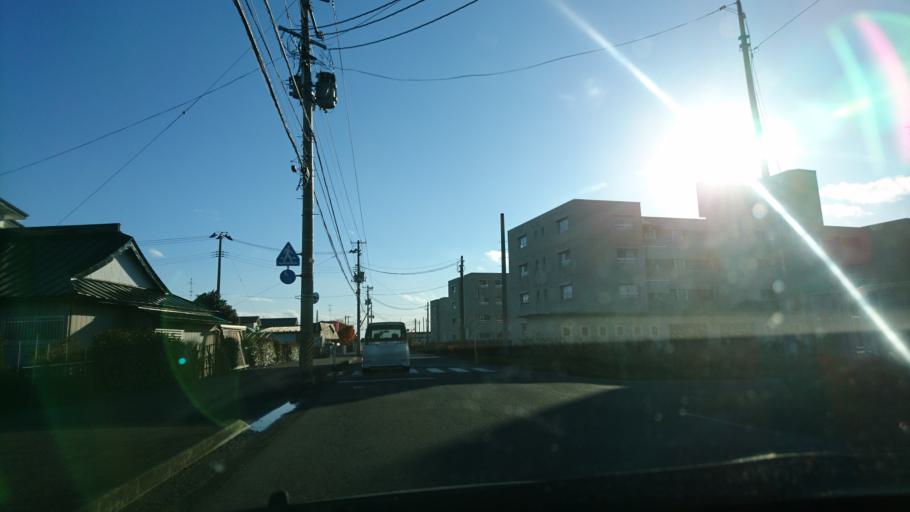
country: JP
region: Iwate
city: Mizusawa
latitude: 39.1149
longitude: 141.1552
